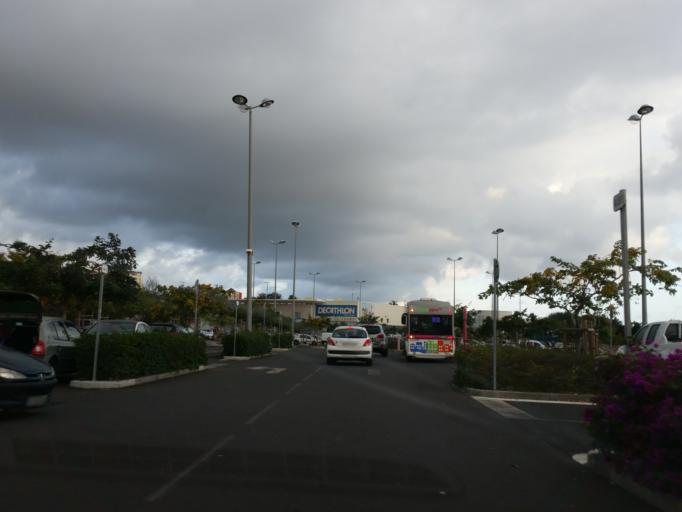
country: RE
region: Reunion
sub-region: Reunion
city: Saint-Pierre
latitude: -21.3281
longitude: 55.4681
